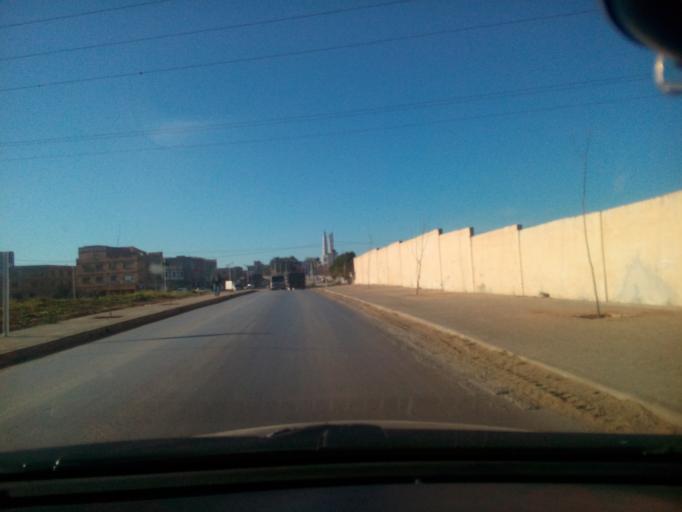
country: DZ
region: Mostaganem
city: Mostaganem
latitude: 35.9223
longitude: 0.1191
